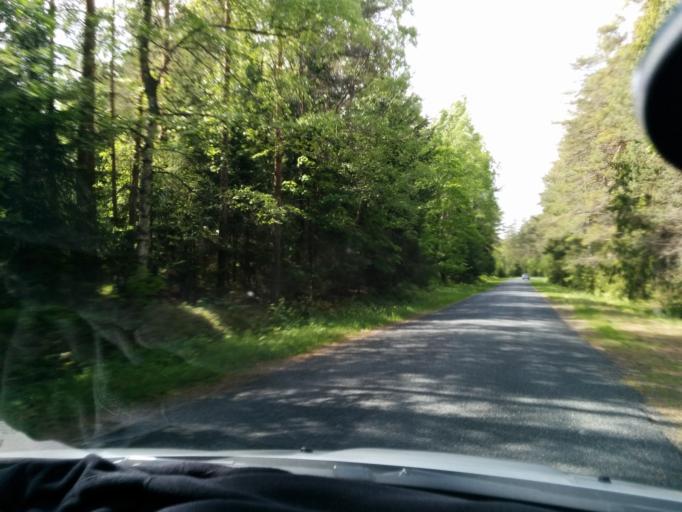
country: EE
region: Harju
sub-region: Loksa linn
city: Loksa
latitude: 59.5727
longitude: 25.6163
